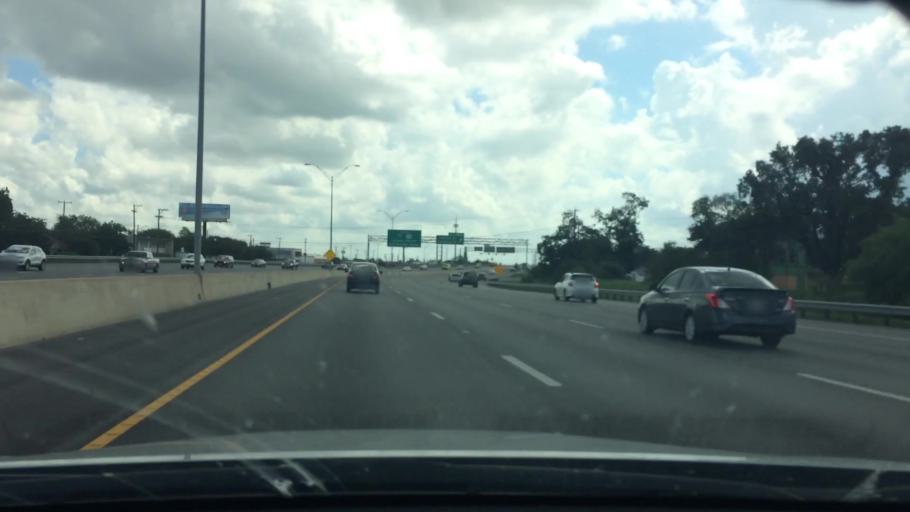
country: US
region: Texas
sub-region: Bexar County
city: San Antonio
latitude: 29.4111
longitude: -98.4800
